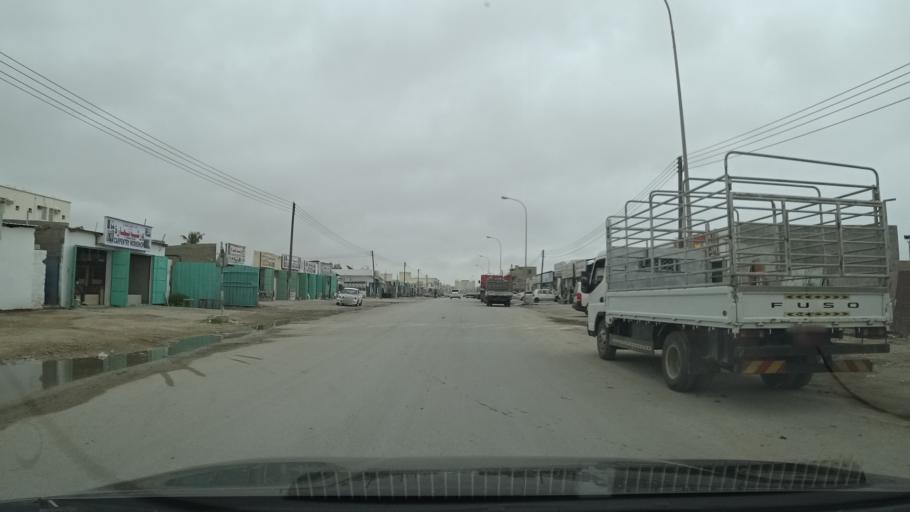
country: OM
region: Zufar
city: Salalah
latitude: 17.0193
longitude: 54.0464
